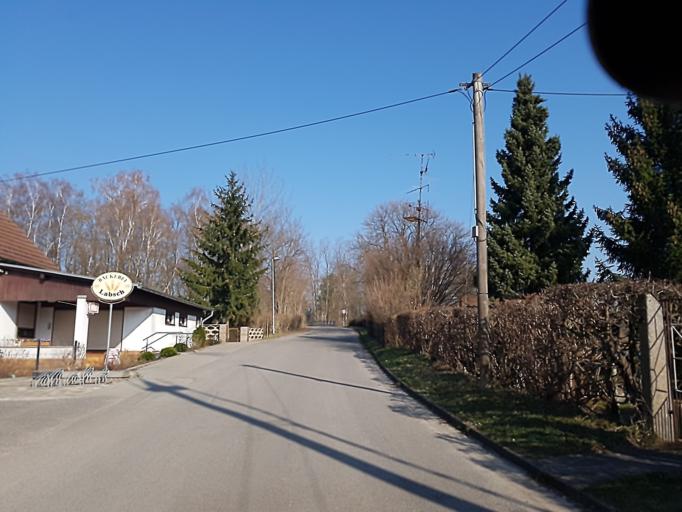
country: DE
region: Brandenburg
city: Tschernitz
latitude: 51.6541
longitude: 14.5769
